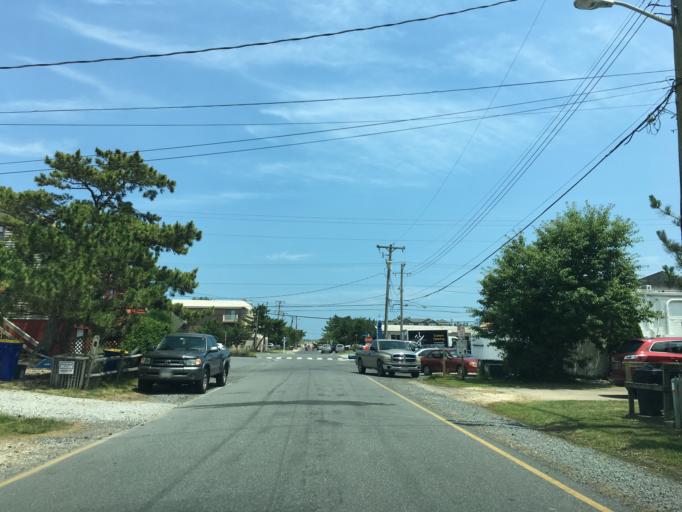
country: US
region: Delaware
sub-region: Sussex County
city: Bethany Beach
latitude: 38.4614
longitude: -75.0530
